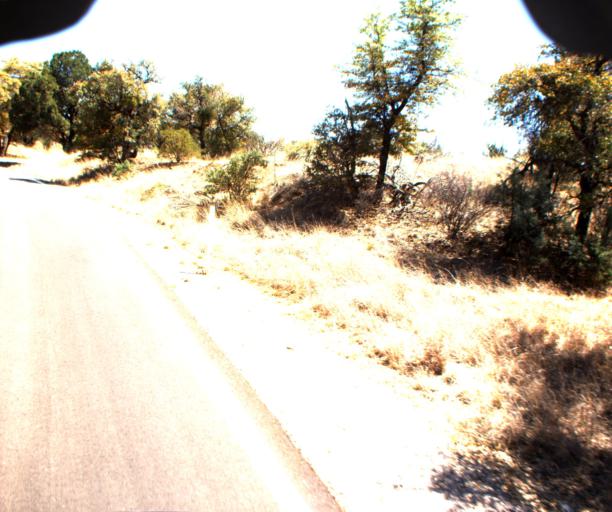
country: US
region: Arizona
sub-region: Cochise County
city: Huachuca City
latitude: 31.5652
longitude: -110.5581
